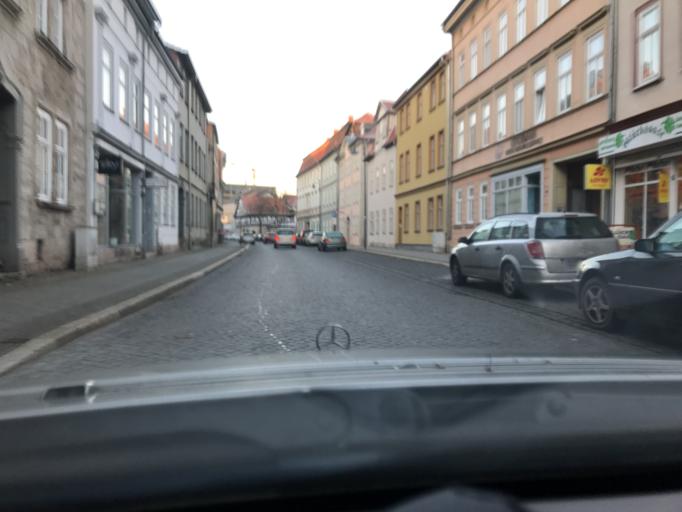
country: DE
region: Thuringia
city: Muehlhausen
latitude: 51.2074
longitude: 10.4568
